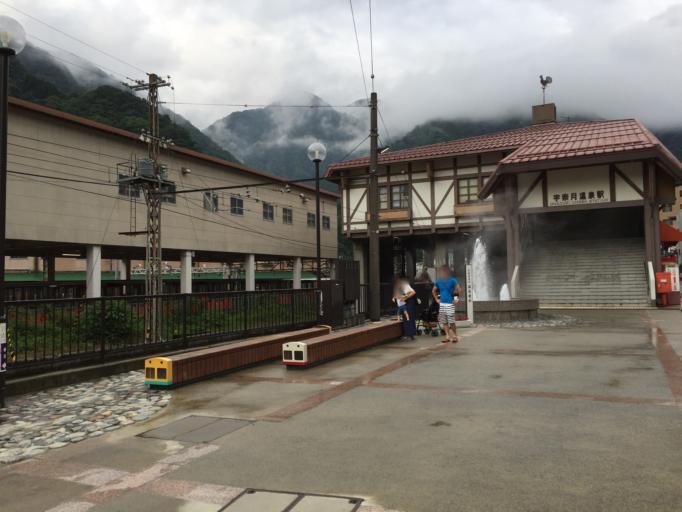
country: JP
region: Toyama
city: Nyuzen
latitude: 36.8158
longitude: 137.5830
